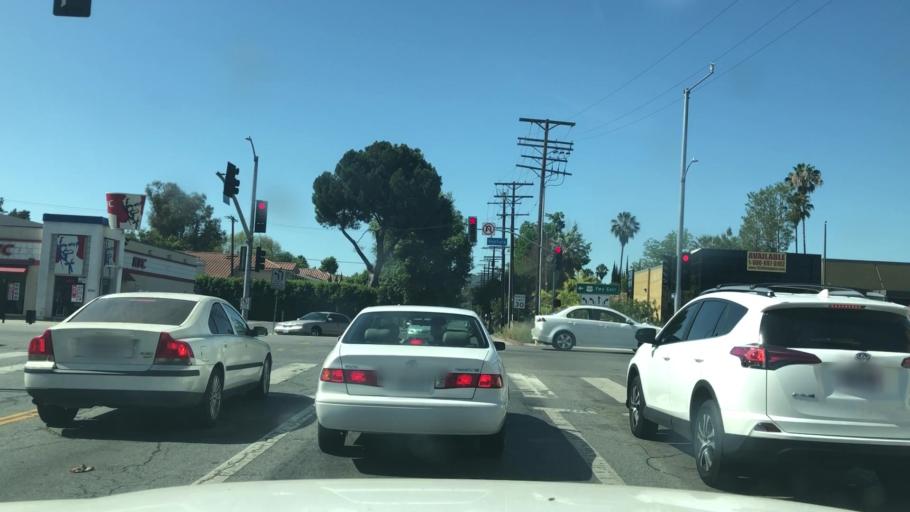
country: US
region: California
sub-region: Los Angeles County
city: Woodland Hills
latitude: 34.1729
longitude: -118.5535
